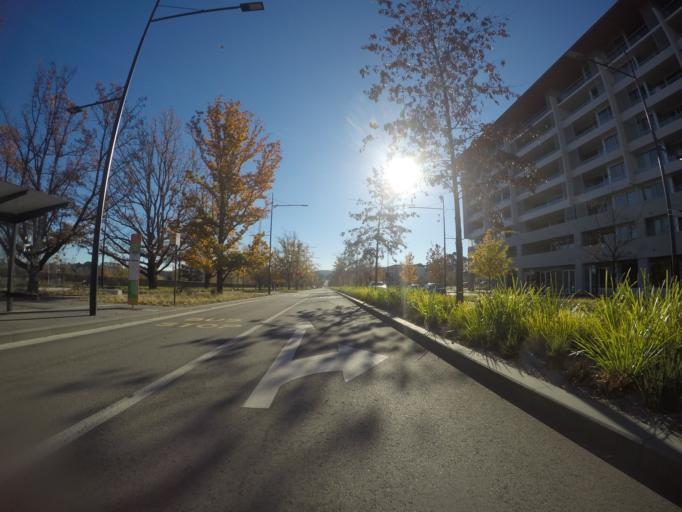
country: AU
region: Australian Capital Territory
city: Canberra
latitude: -35.2881
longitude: 149.1390
